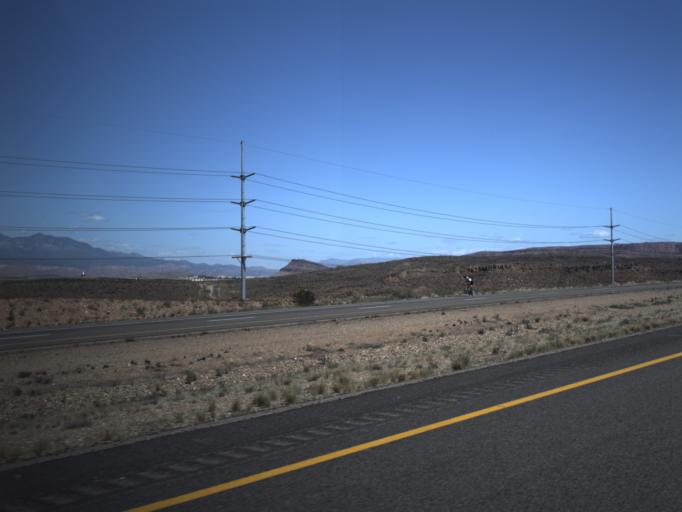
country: US
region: Utah
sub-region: Washington County
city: Saint George
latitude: 37.0060
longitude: -113.5221
